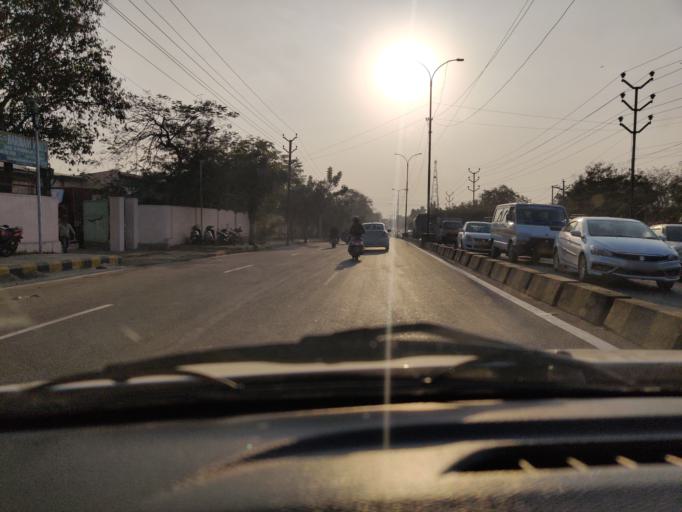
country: IN
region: Telangana
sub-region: Rangareddi
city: Uppal Kalan
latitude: 17.4398
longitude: 78.5622
